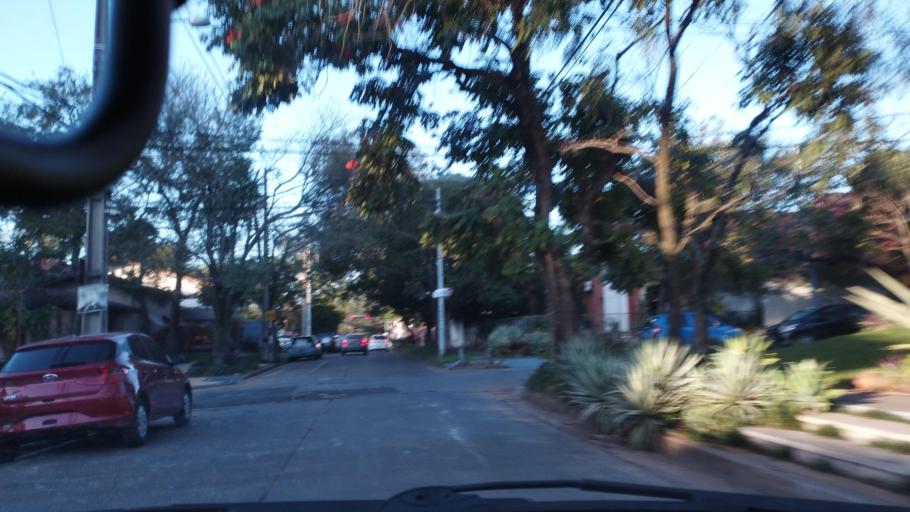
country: PY
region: Central
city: Lambare
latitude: -25.2977
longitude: -57.5745
